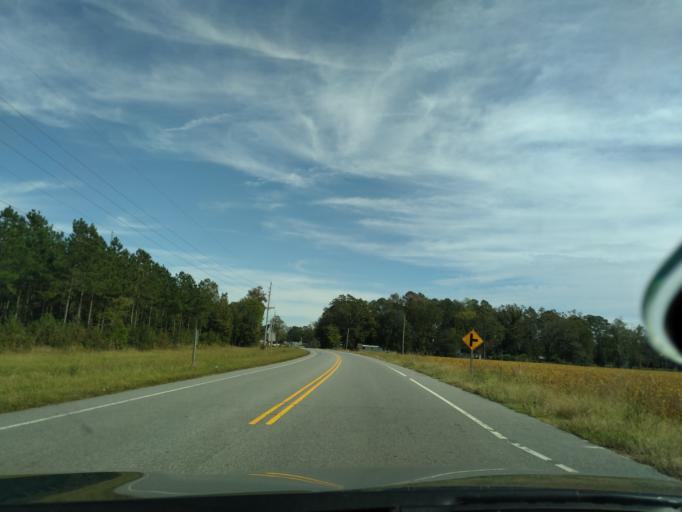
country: US
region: North Carolina
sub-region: Beaufort County
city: River Road
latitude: 35.5124
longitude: -76.9085
